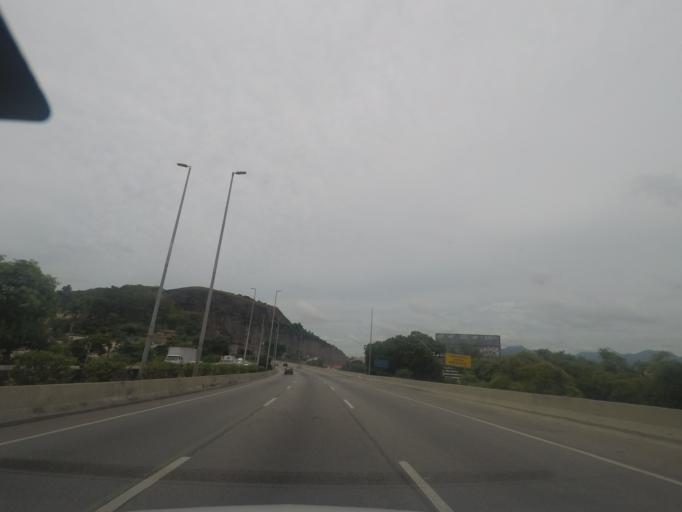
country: BR
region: Rio de Janeiro
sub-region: Sao Joao De Meriti
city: Sao Joao de Meriti
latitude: -22.9267
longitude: -43.3413
